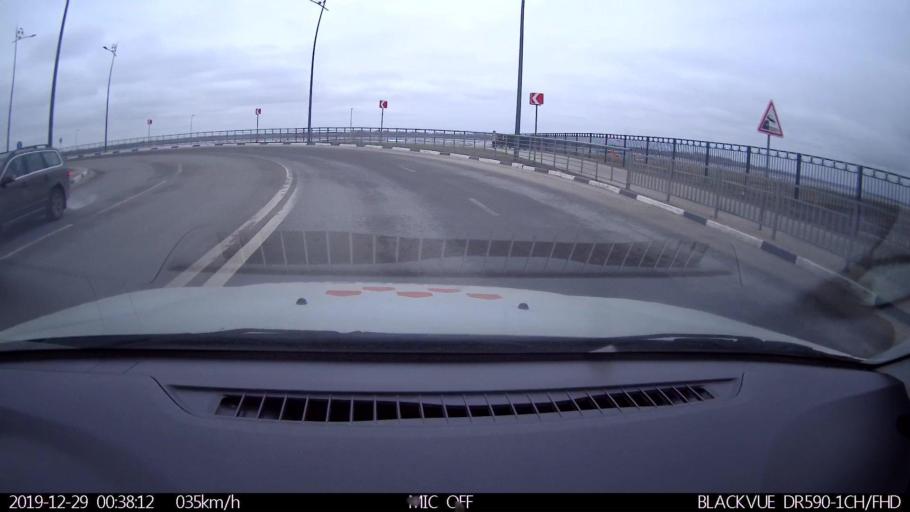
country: RU
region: Nizjnij Novgorod
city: Nizhniy Novgorod
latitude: 56.3355
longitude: 43.9719
